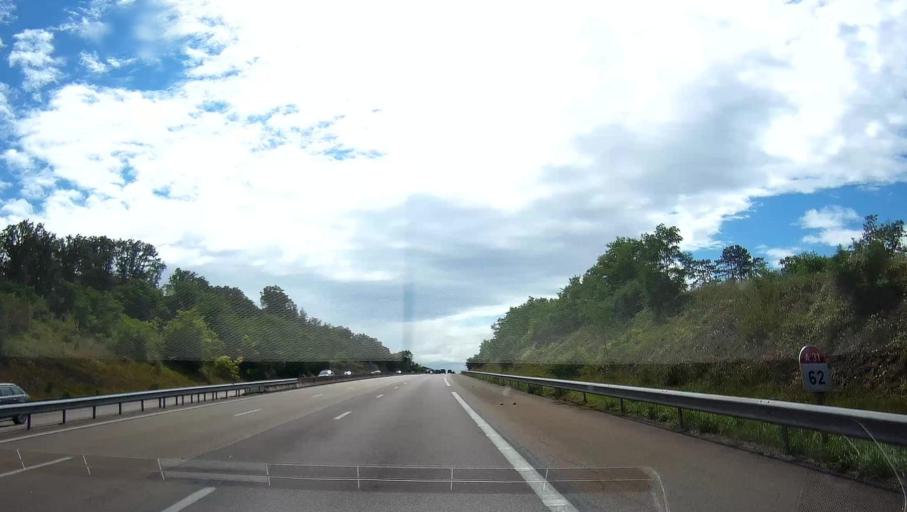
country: FR
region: Bourgogne
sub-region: Departement de la Cote-d'Or
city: Marcilly-sur-Tille
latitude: 47.4688
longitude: 5.1854
